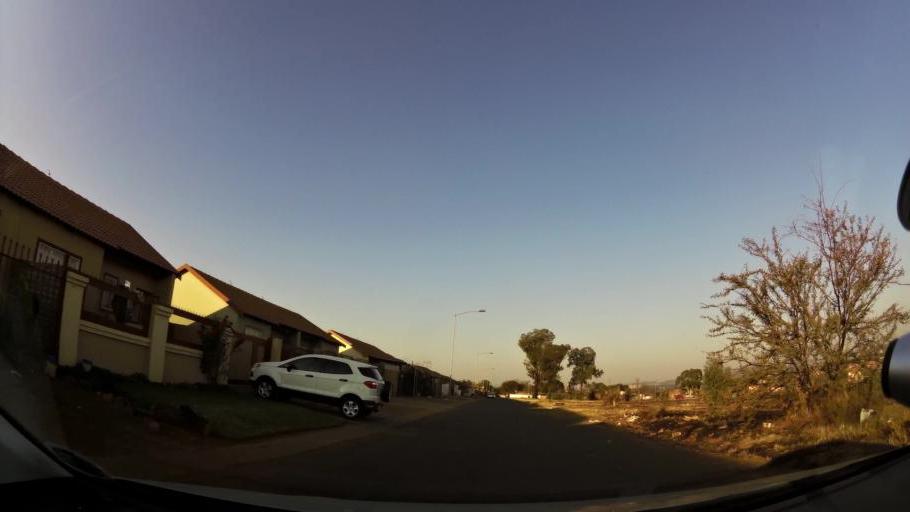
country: ZA
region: Gauteng
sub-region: City of Tshwane Metropolitan Municipality
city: Pretoria
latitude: -25.7439
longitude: 28.1074
